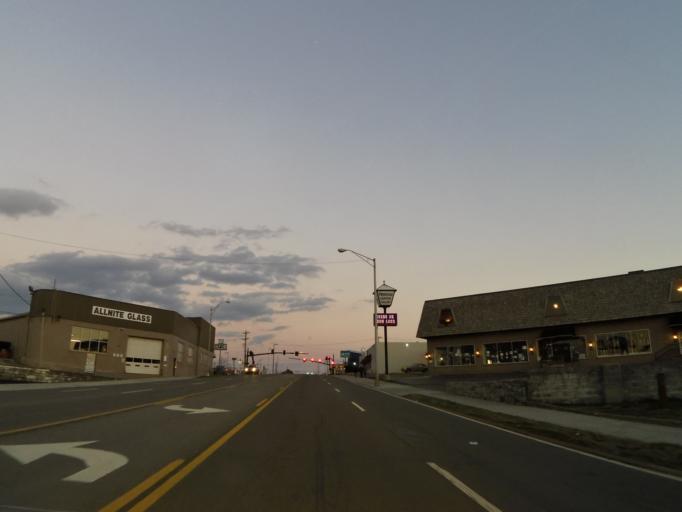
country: US
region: Tennessee
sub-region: Davidson County
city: Nashville
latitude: 36.1530
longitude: -86.7748
